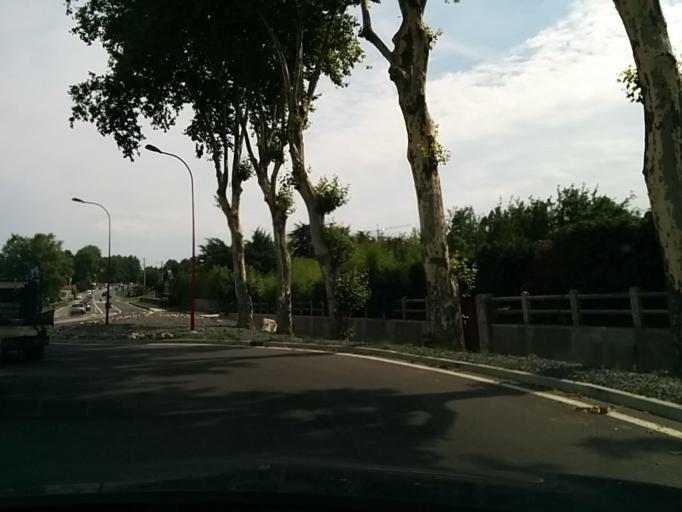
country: FR
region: Aquitaine
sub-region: Departement des Pyrenees-Atlantiques
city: Ciboure
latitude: 43.3721
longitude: -1.6813
